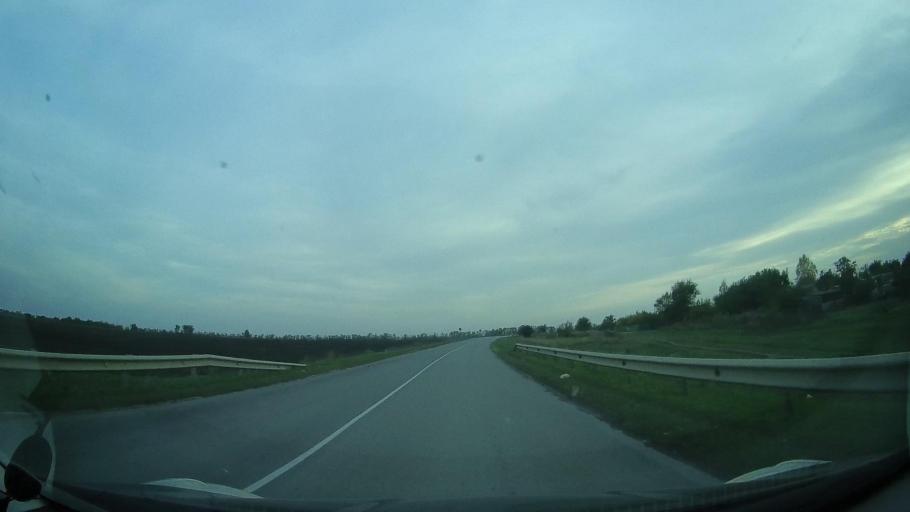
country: RU
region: Rostov
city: Kirovskaya
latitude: 47.0331
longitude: 39.9813
